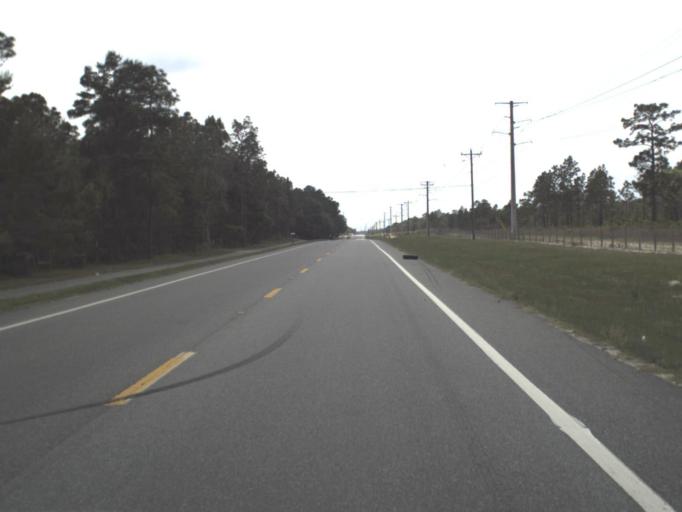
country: US
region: Florida
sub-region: Clay County
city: Keystone Heights
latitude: 29.8250
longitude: -81.9900
